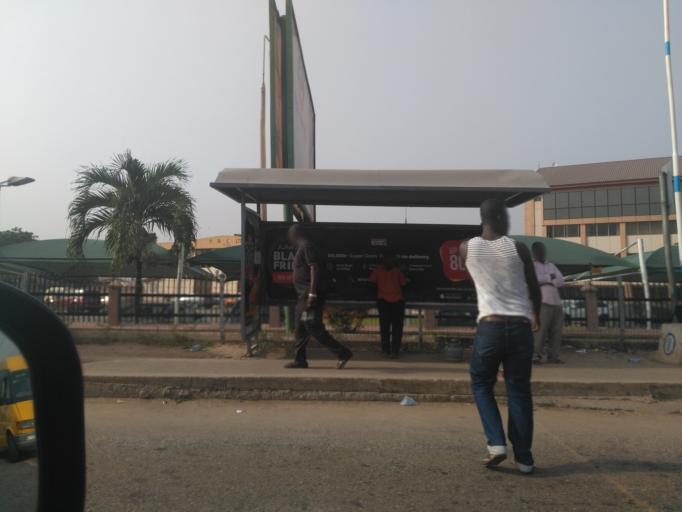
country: GH
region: Greater Accra
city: Dome
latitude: 5.6072
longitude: -0.2072
